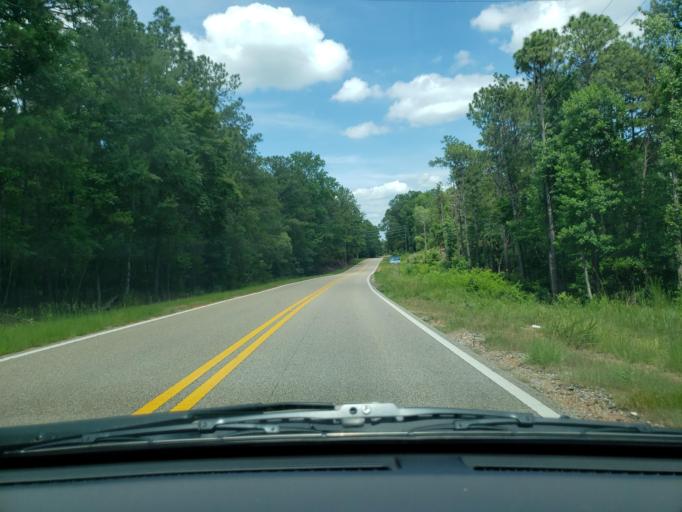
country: US
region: Alabama
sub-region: Elmore County
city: Eclectic
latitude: 32.6718
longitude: -85.9205
